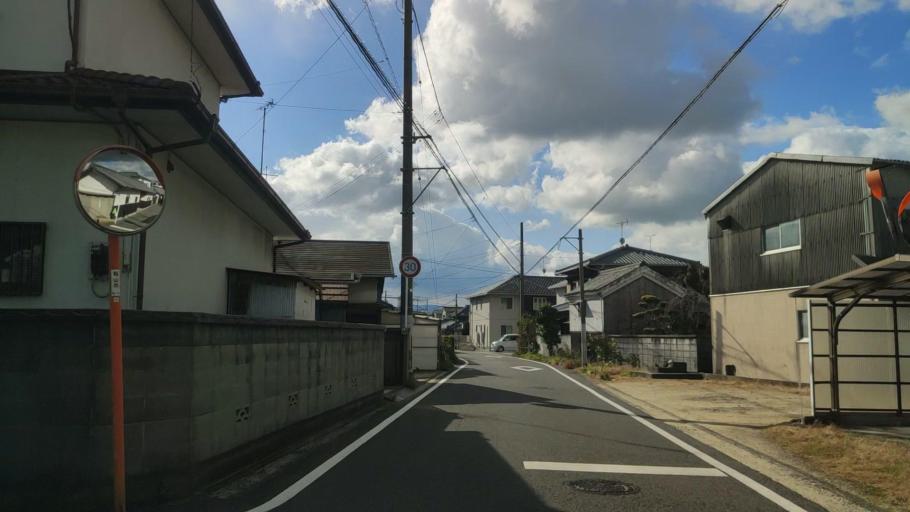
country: JP
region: Ehime
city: Masaki-cho
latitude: 33.8261
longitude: 132.7086
